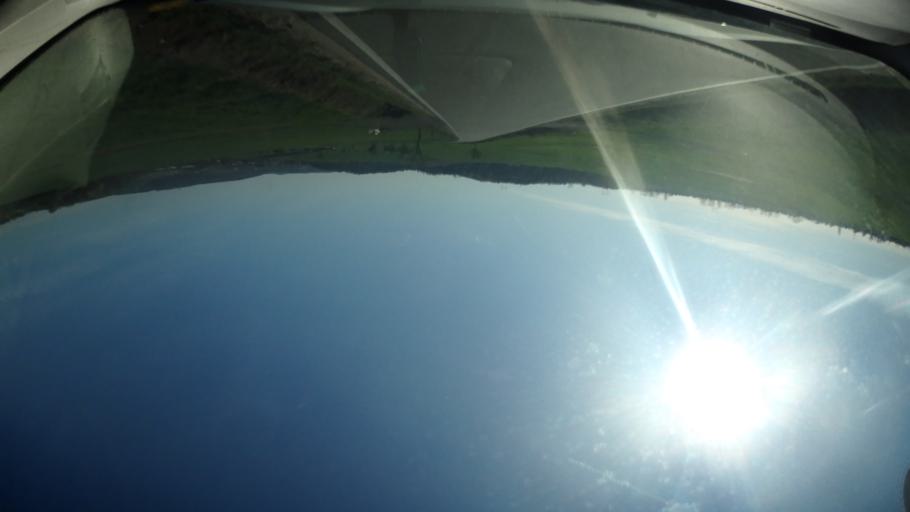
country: CZ
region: South Moravian
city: Moravany
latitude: 49.1507
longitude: 16.5622
